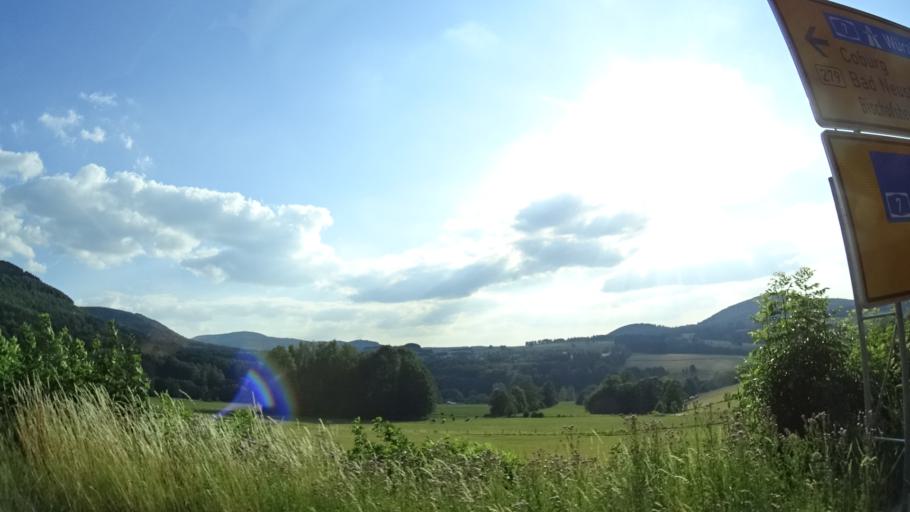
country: DE
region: Hesse
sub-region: Regierungsbezirk Kassel
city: Gersfeld
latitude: 50.4313
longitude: 9.9294
